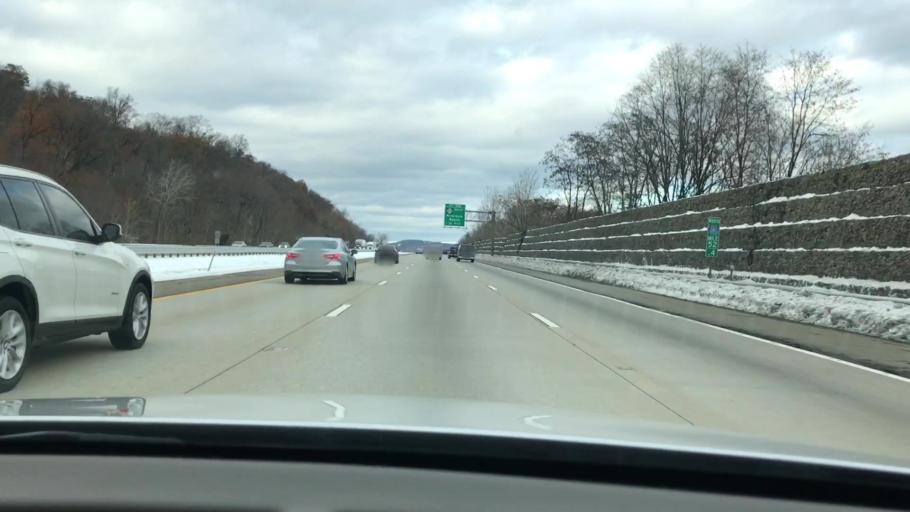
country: US
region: New Jersey
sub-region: Morris County
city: Riverdale
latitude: 40.9791
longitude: -74.3162
